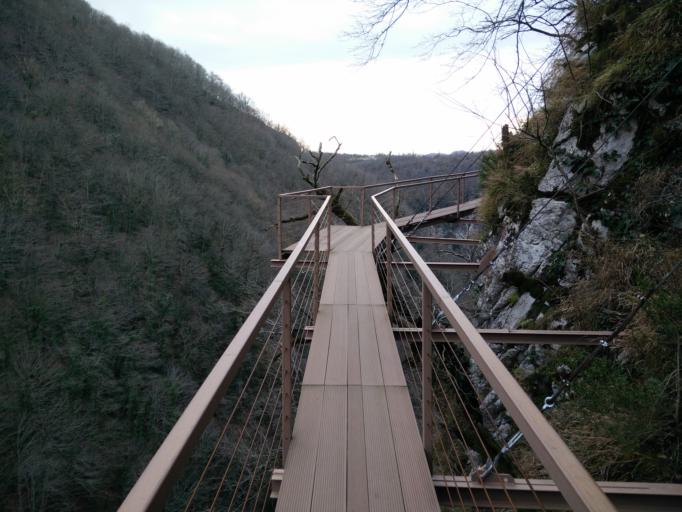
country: GE
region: Imereti
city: Tsqaltubo
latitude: 42.4529
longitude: 42.5503
